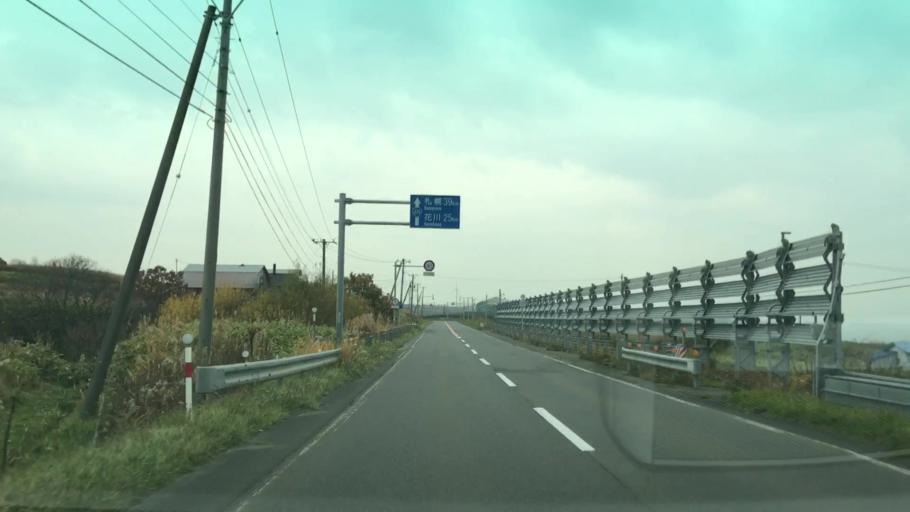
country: JP
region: Hokkaido
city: Ishikari
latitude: 43.3414
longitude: 141.4233
